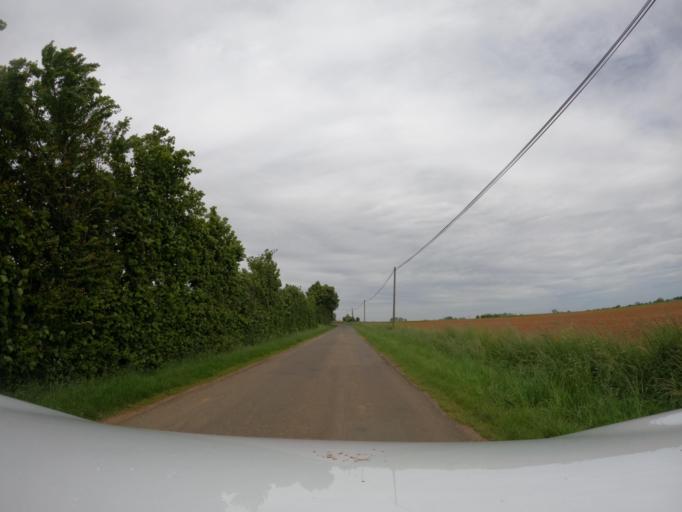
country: FR
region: Pays de la Loire
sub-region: Departement de la Vendee
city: Saint-Hilaire-des-Loges
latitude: 46.4845
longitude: -0.6409
